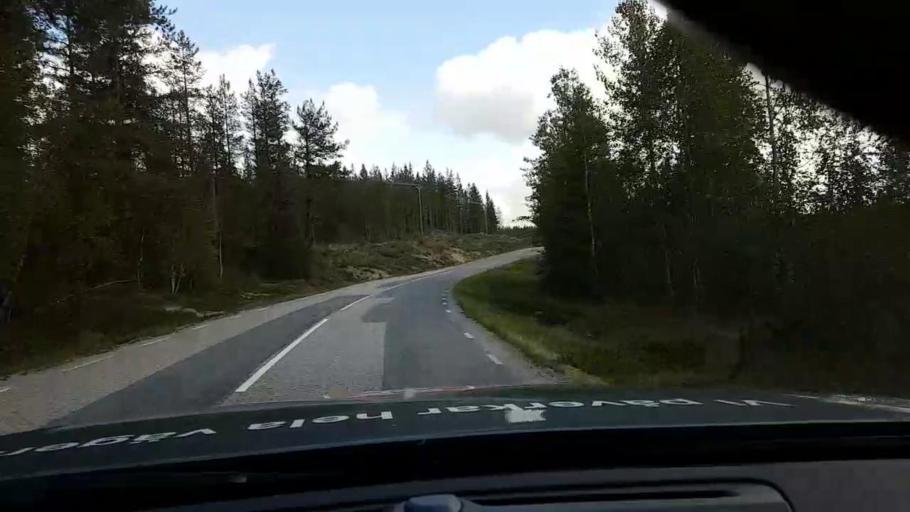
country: SE
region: Vaesterbotten
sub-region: Asele Kommun
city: Asele
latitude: 63.8016
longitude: 17.5506
